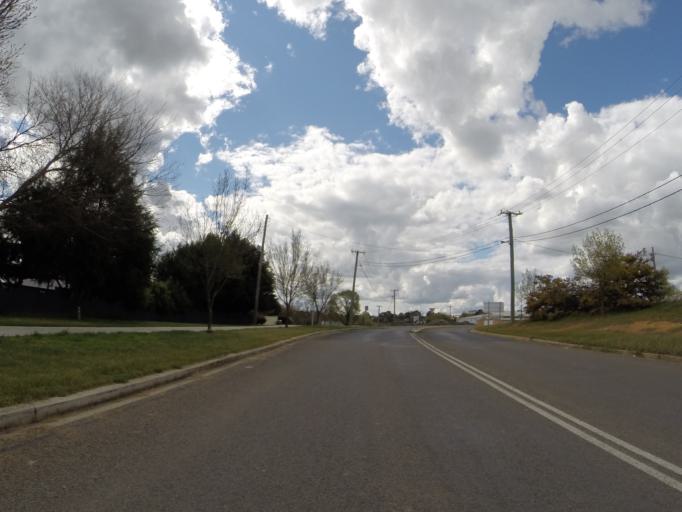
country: AU
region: New South Wales
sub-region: Yass Valley
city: Yass
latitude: -34.8558
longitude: 148.9192
